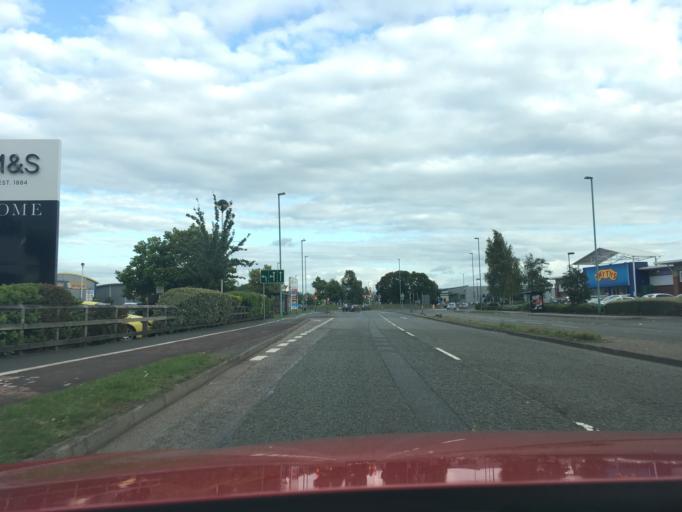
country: GB
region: England
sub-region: Gloucestershire
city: Swindon
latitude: 51.9150
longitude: -2.1013
